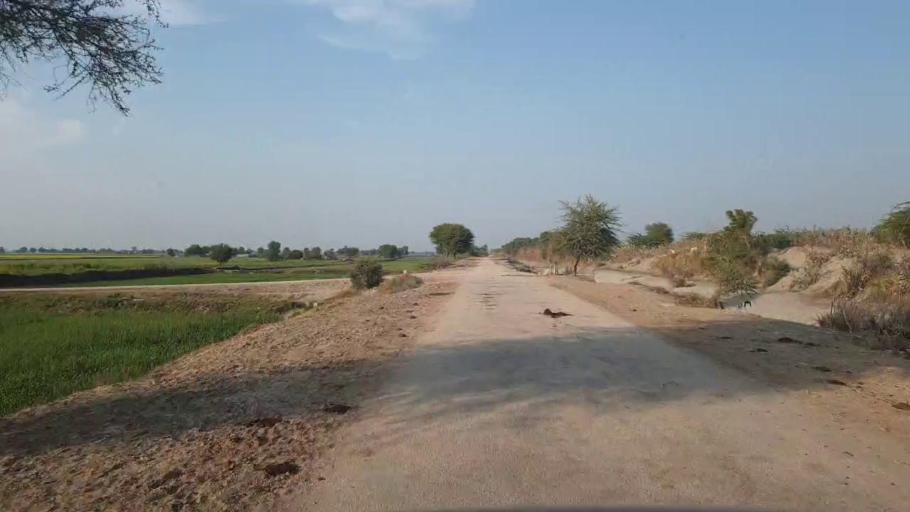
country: PK
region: Sindh
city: Shahpur Chakar
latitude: 26.1653
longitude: 68.6405
